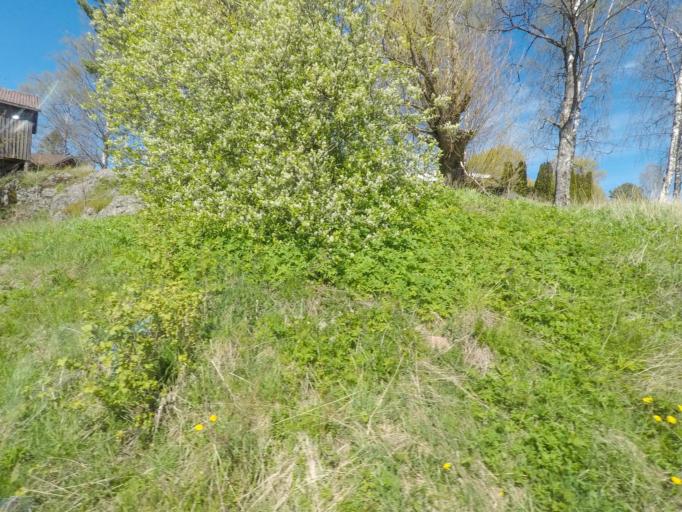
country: FI
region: Uusimaa
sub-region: Helsinki
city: Sammatti
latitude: 60.4756
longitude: 23.8238
